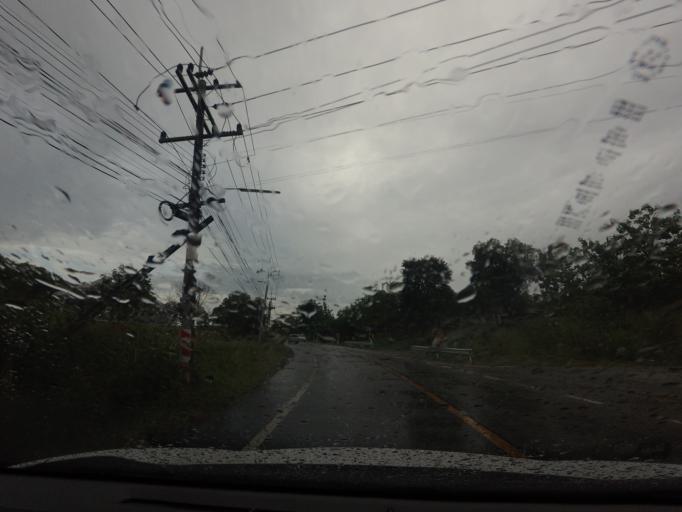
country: TH
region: Chon Buri
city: Sattahip
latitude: 12.6962
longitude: 100.9536
